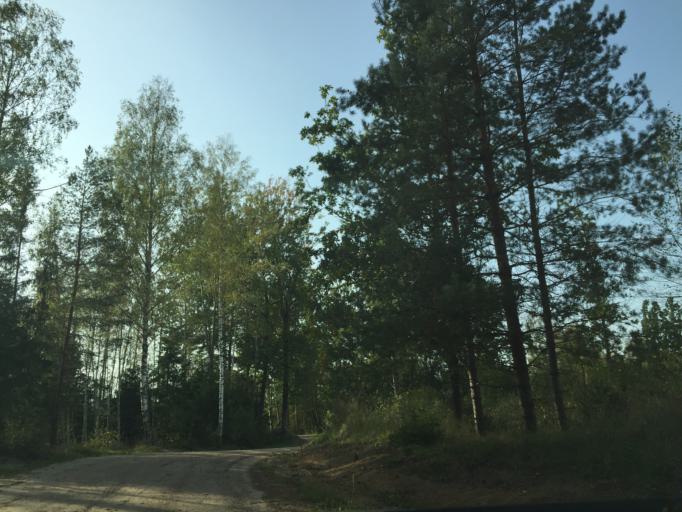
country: LV
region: Garkalne
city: Garkalne
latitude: 56.9729
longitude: 24.4211
